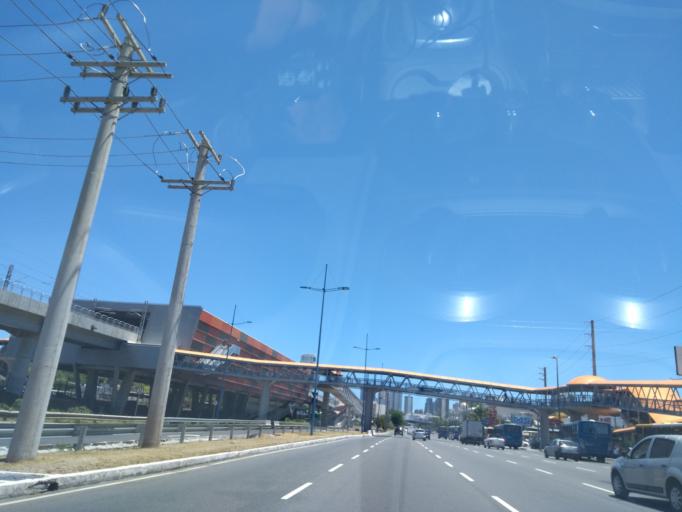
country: BR
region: Bahia
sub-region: Salvador
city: Salvador
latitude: -12.9780
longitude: -38.4726
